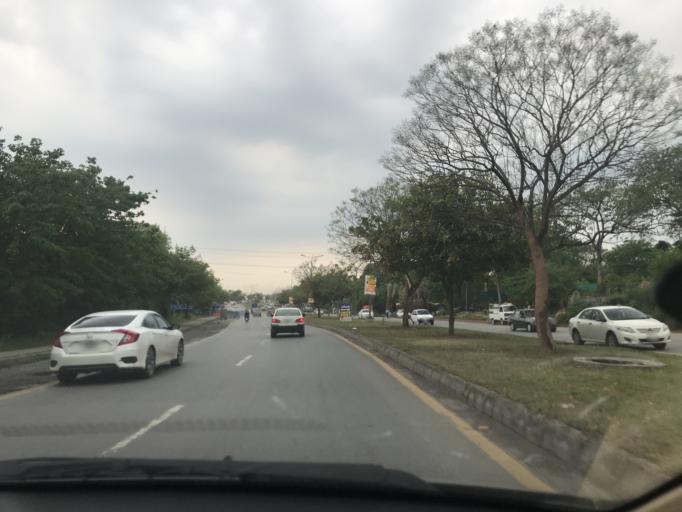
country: PK
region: Islamabad
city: Islamabad
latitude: 33.6892
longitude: 73.1149
